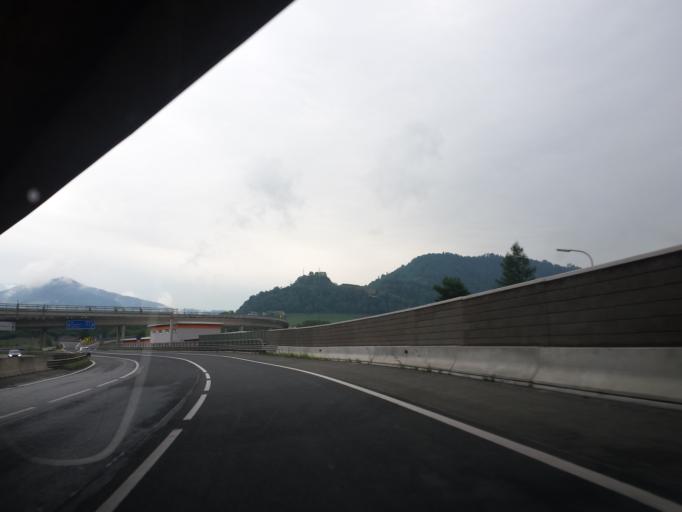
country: AT
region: Styria
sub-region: Politischer Bezirk Bruck-Muerzzuschlag
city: Bruck an der Mur
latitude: 47.4042
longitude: 15.2851
